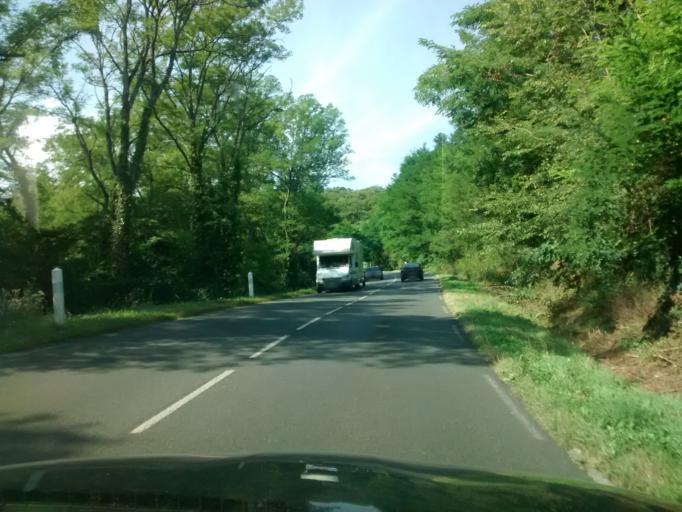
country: FR
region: Aquitaine
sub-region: Departement de la Dordogne
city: Sarlat-la-Caneda
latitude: 44.8657
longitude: 1.2037
